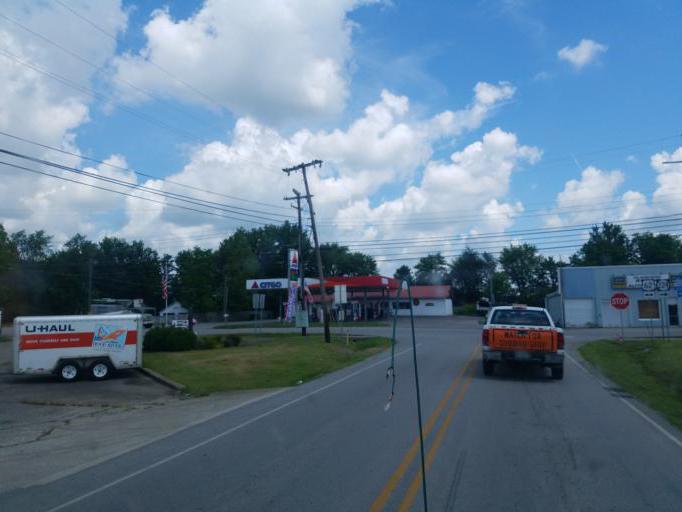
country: US
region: Kentucky
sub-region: Grayson County
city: Leitchfield
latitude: 37.4951
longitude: -86.2254
